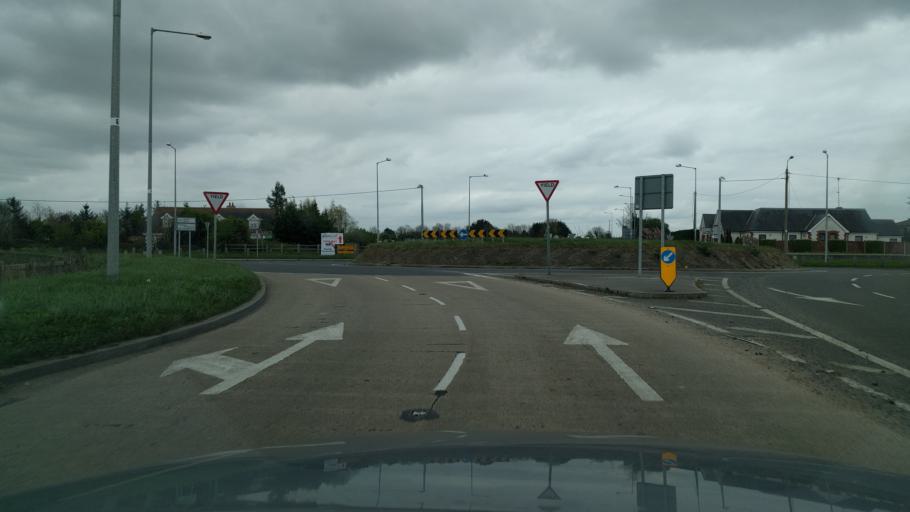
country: IE
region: Leinster
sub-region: Fingal County
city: Blanchardstown
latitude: 53.4455
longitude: -6.3418
